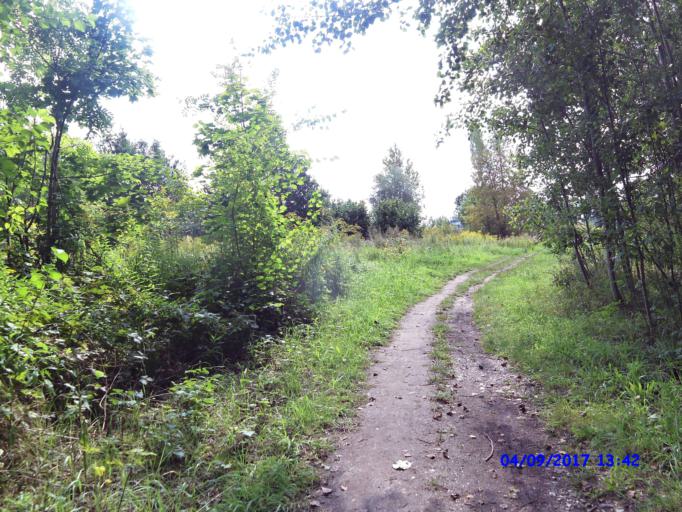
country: DE
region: Saxony
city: Taucha
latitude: 51.3522
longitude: 12.4728
